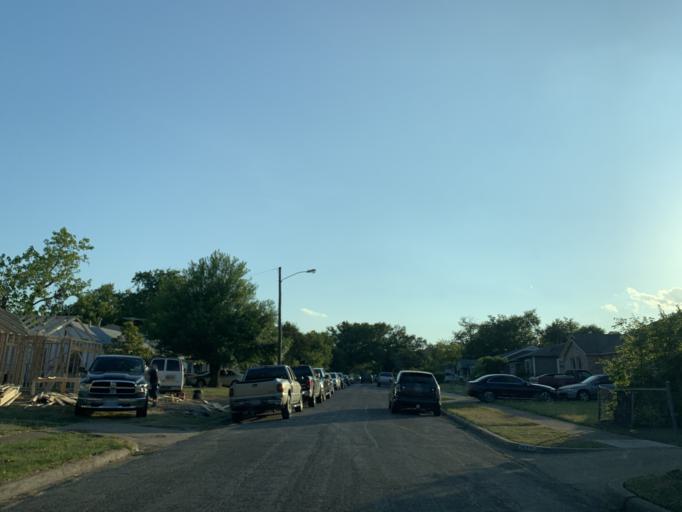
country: US
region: Texas
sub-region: Dallas County
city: Dallas
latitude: 32.7102
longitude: -96.7848
